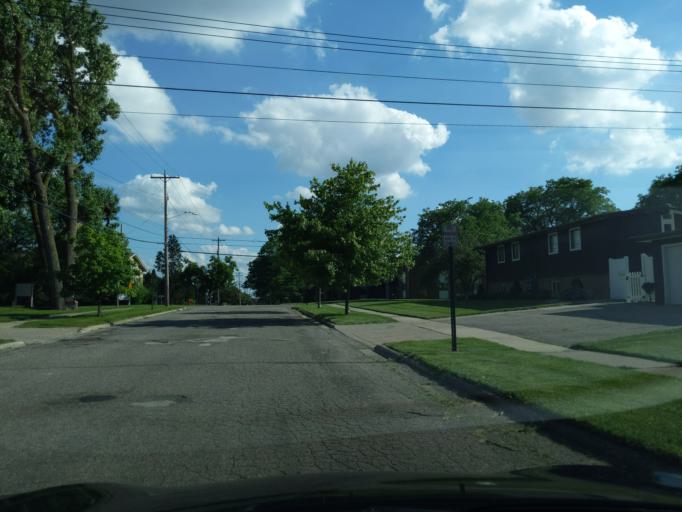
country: US
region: Michigan
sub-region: Ingham County
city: East Lansing
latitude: 42.7471
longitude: -84.5095
